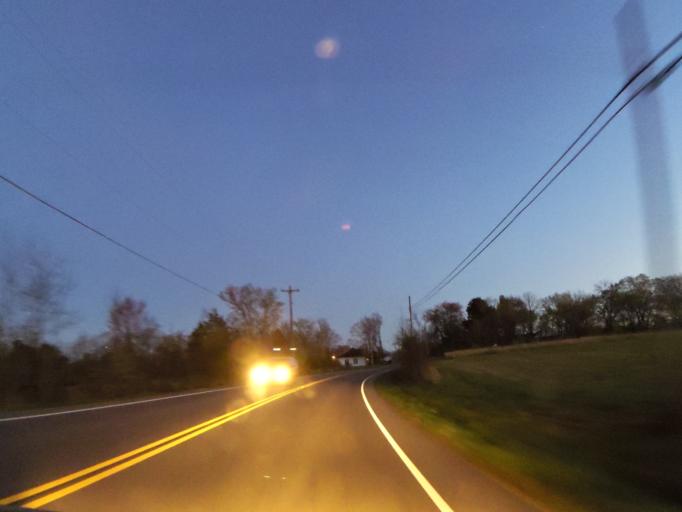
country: US
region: Tennessee
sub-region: Robertson County
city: Greenbrier
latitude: 36.3564
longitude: -86.8816
